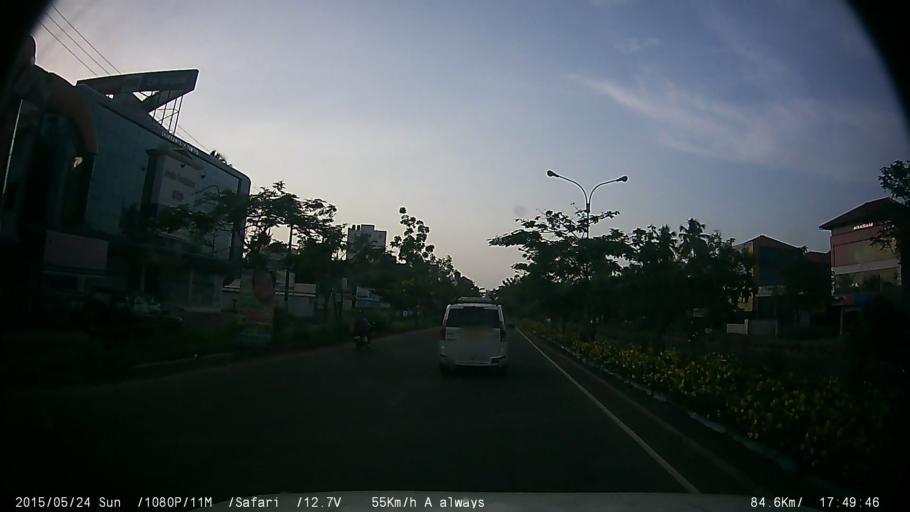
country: IN
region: Kerala
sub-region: Ernakulam
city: Cochin
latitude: 9.9927
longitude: 76.3150
